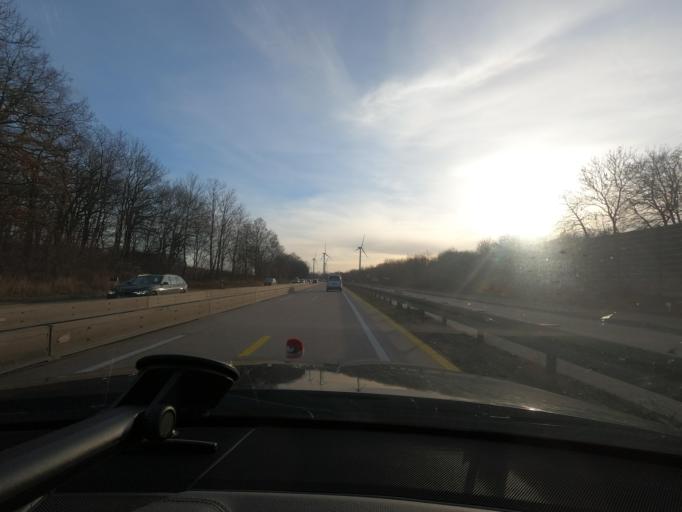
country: DE
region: Lower Saxony
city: Harsum
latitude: 52.2122
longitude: 9.9341
